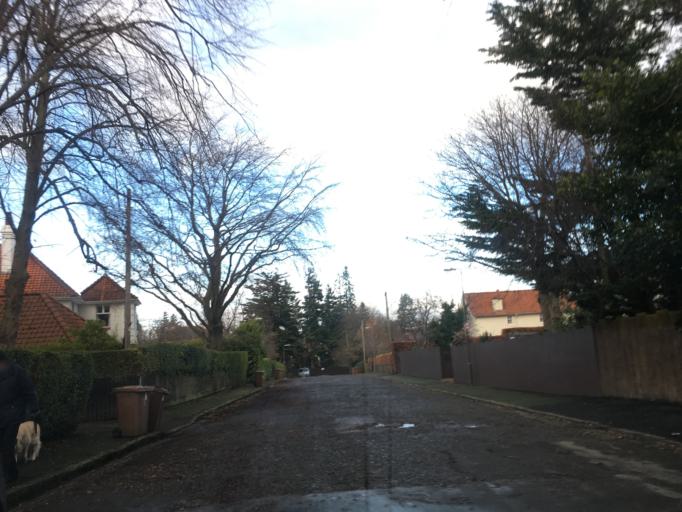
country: GB
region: Scotland
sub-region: Edinburgh
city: Colinton
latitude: 55.9034
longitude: -3.2584
